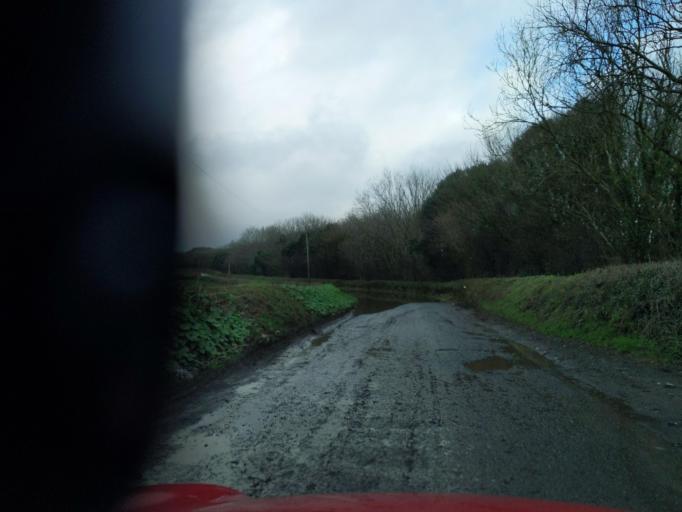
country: GB
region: England
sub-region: Devon
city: Yelverton
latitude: 50.4436
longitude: -4.1256
